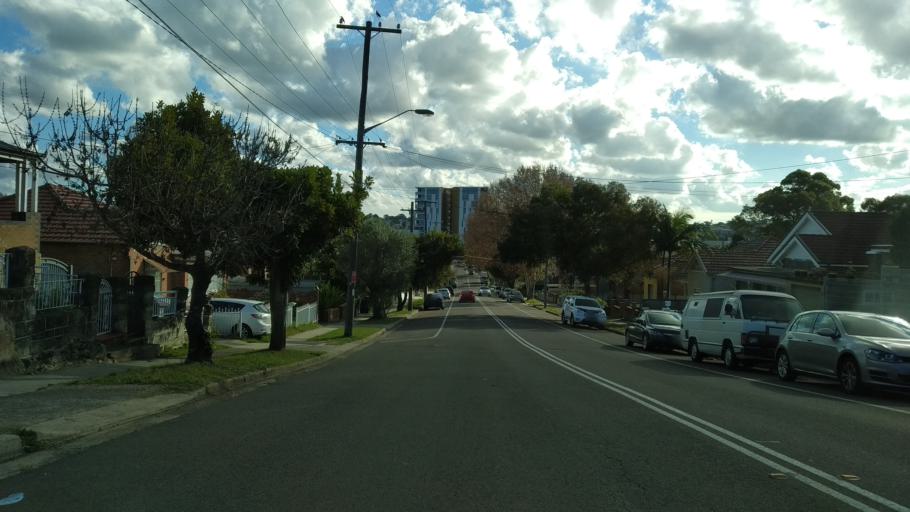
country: AU
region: New South Wales
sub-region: Rockdale
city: Banksia
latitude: -33.9489
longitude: 151.1432
